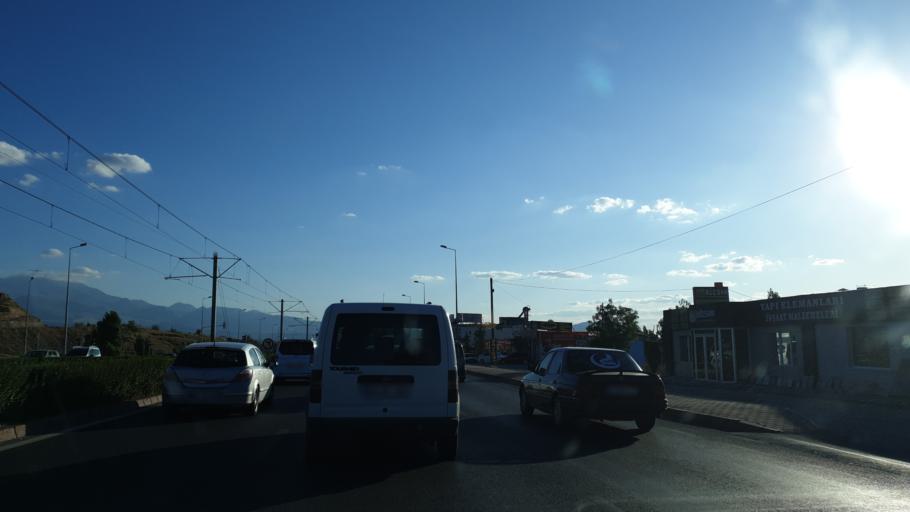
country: TR
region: Kayseri
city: Kocasinan
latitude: 38.7709
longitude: 35.5689
